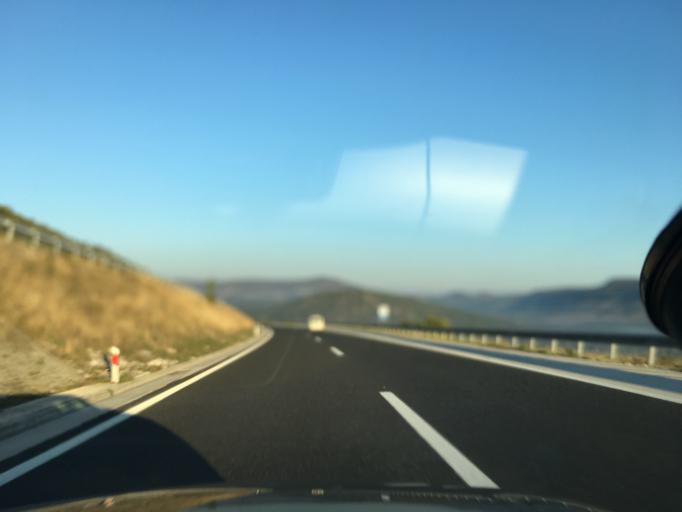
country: HR
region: Splitsko-Dalmatinska
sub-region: Grad Trogir
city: Trogir
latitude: 43.6303
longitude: 16.2300
